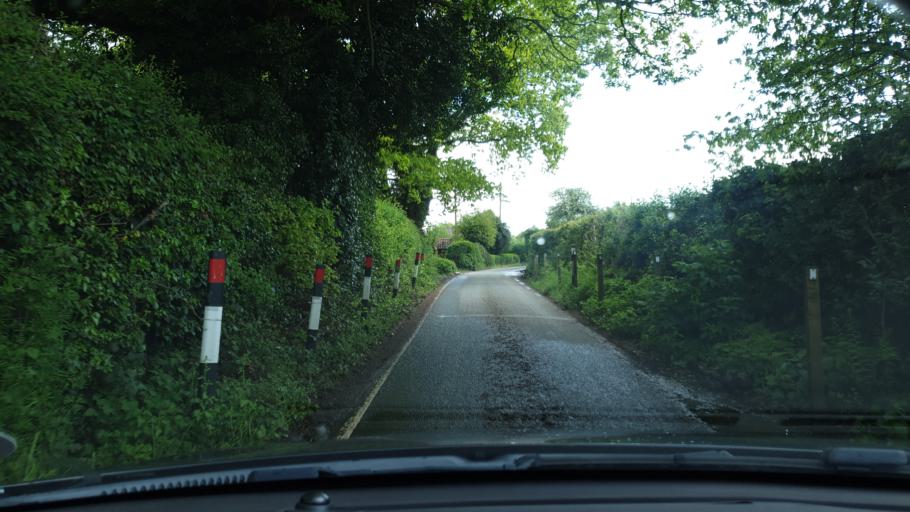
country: GB
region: England
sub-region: Essex
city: Great Bentley
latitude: 51.8784
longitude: 1.0567
